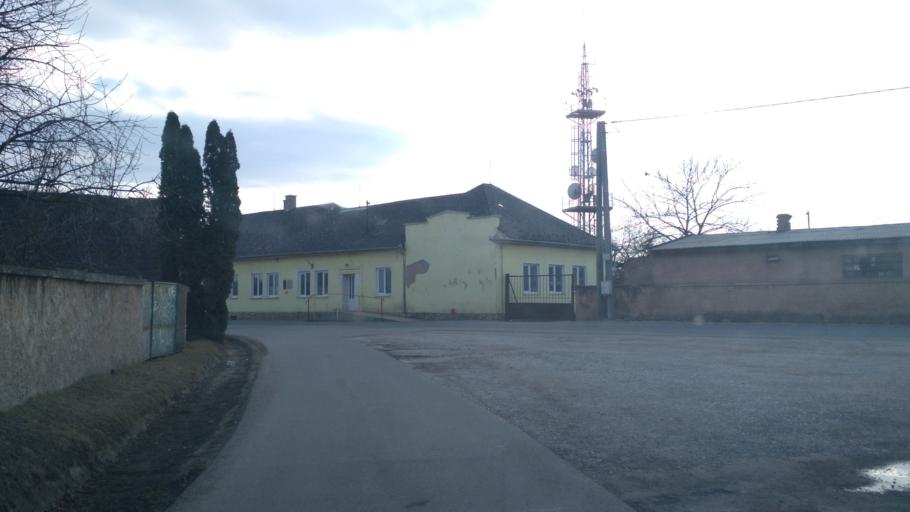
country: SK
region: Kosicky
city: Medzev
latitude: 48.6019
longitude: 20.8783
